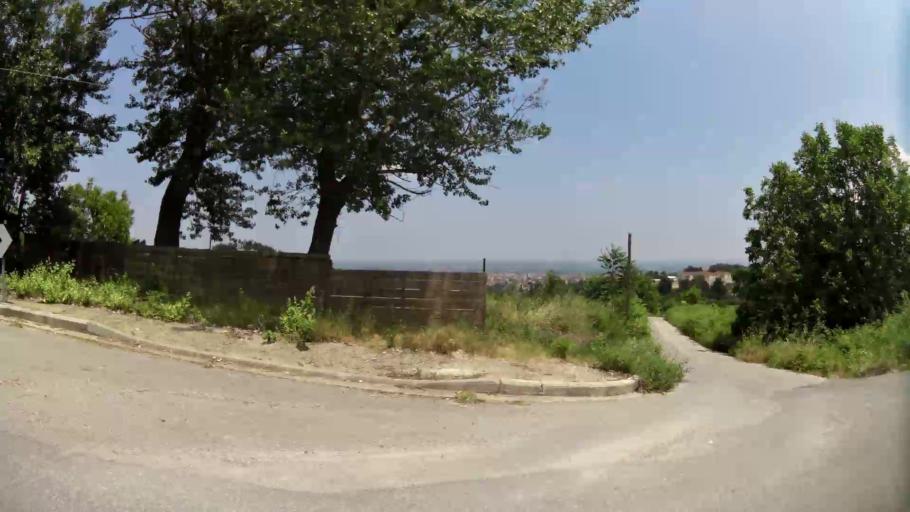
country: GR
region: Central Macedonia
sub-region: Nomos Imathias
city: Veroia
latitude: 40.5162
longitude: 22.1856
